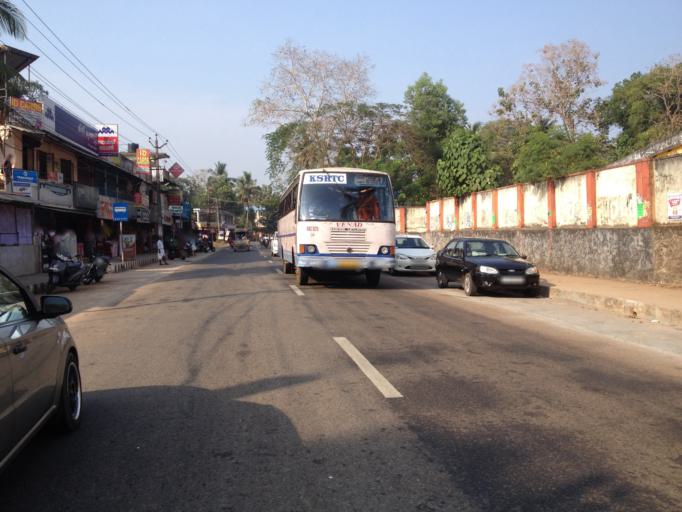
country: IN
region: Kerala
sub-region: Pattanamtitta
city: Adur
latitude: 9.1605
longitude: 76.7190
